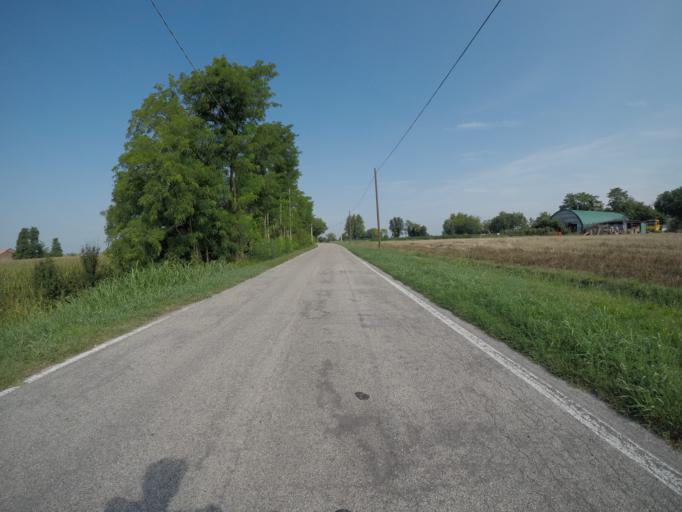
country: IT
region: Veneto
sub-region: Provincia di Rovigo
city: Villanova del Ghebbo Canton
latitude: 45.0592
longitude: 11.6272
